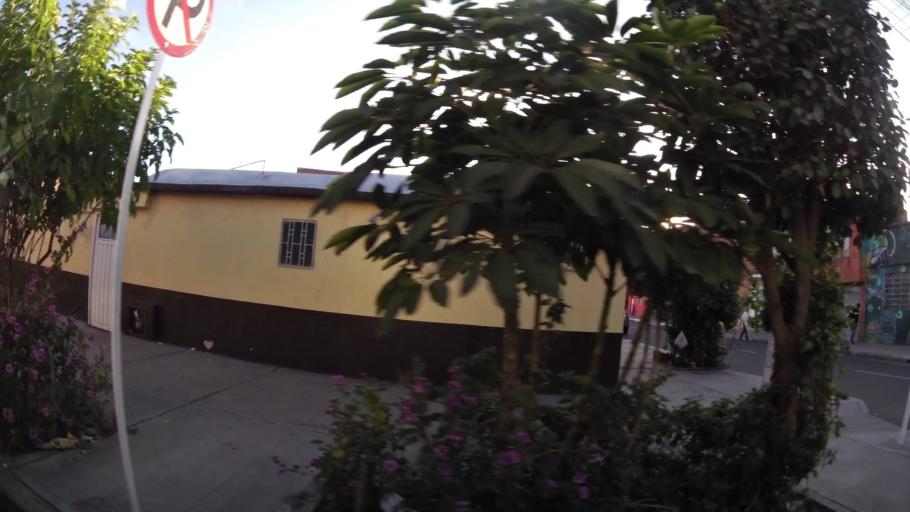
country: CO
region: Bogota D.C.
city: Bogota
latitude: 4.5604
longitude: -74.1267
